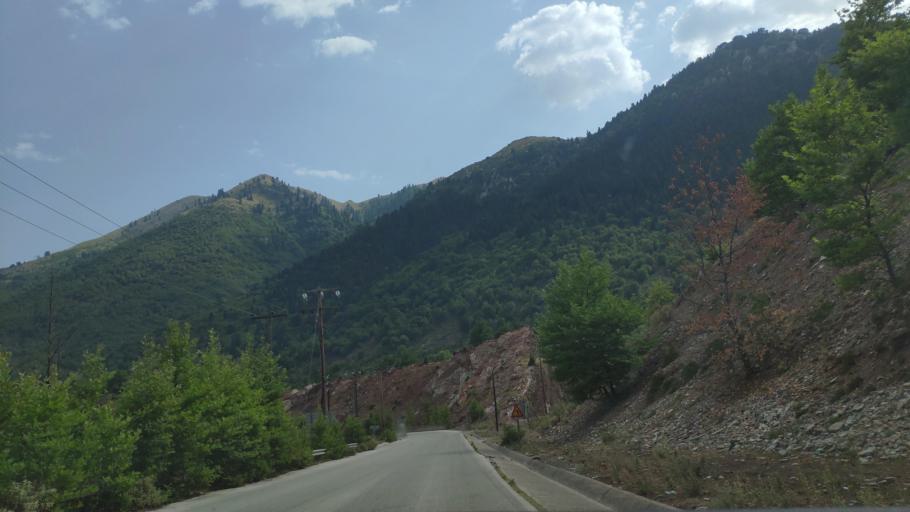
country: GR
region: Epirus
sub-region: Nomos Artas
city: Voulgareli
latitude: 39.4297
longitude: 21.2492
